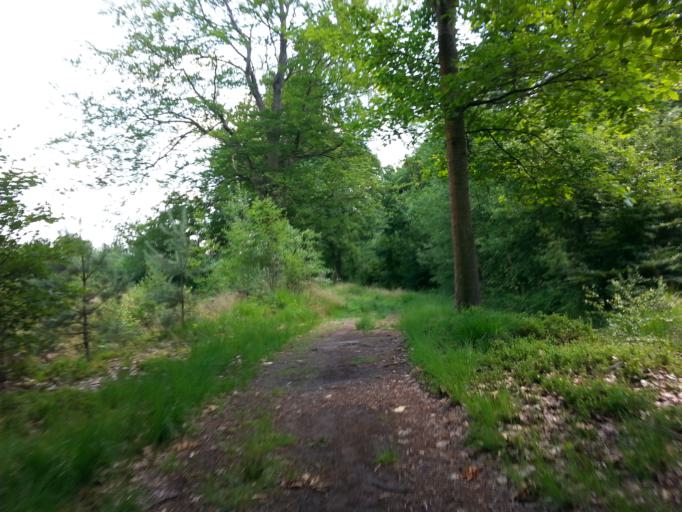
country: NL
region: Utrecht
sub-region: Gemeente Amersfoort
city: Randenbroek
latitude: 52.1167
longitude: 5.3902
